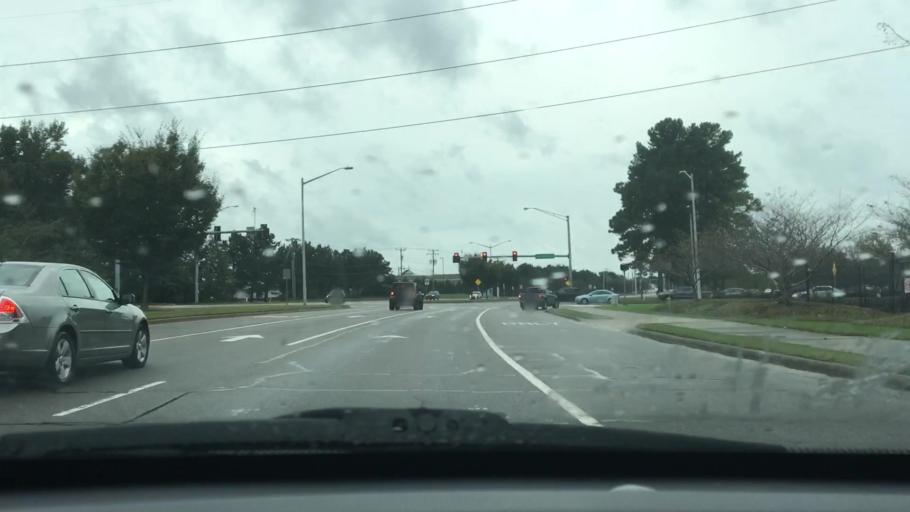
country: US
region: Virginia
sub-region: City of Virginia Beach
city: Virginia Beach
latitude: 36.7796
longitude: -76.0848
